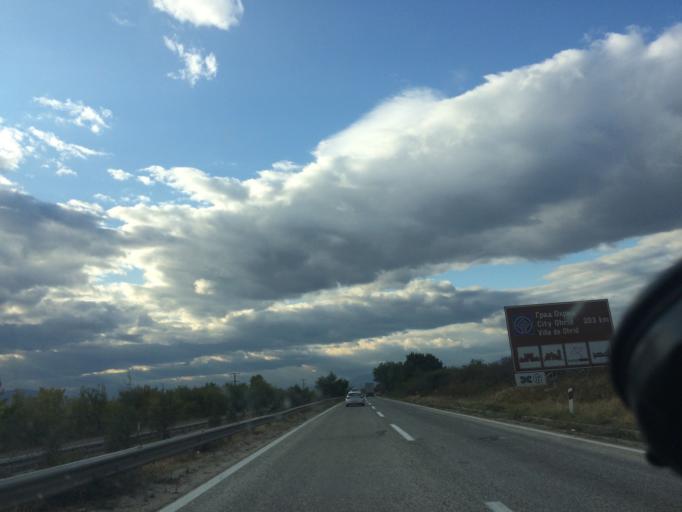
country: MK
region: Petrovec
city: Petrovec
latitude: 41.9077
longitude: 21.6508
